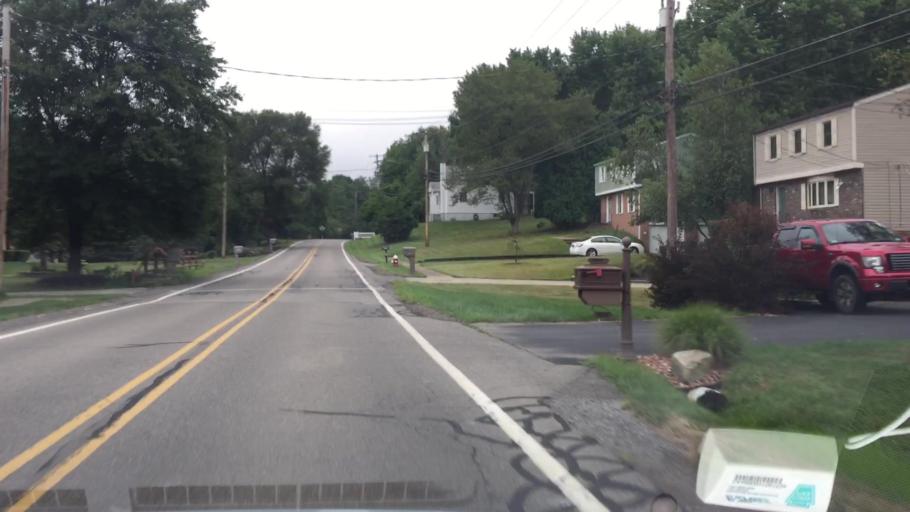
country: US
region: Pennsylvania
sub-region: Allegheny County
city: Franklin Park
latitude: 40.6068
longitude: -80.0757
